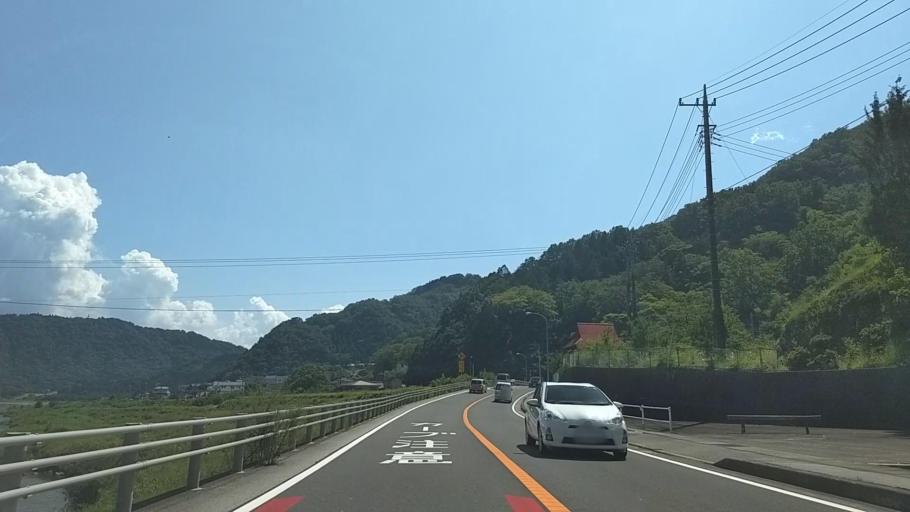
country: JP
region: Yamanashi
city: Ryuo
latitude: 35.5269
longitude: 138.4499
